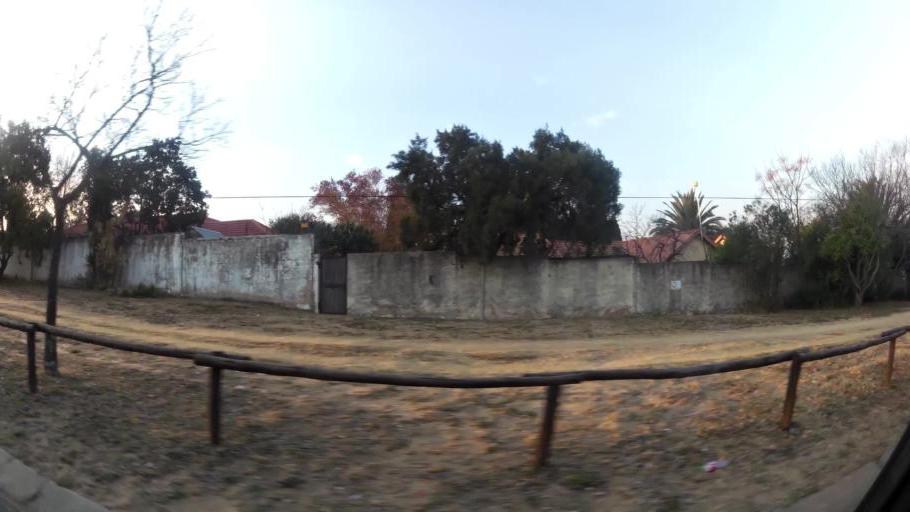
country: ZA
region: Gauteng
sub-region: City of Johannesburg Metropolitan Municipality
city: Diepsloot
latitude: -26.0177
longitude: 28.0355
